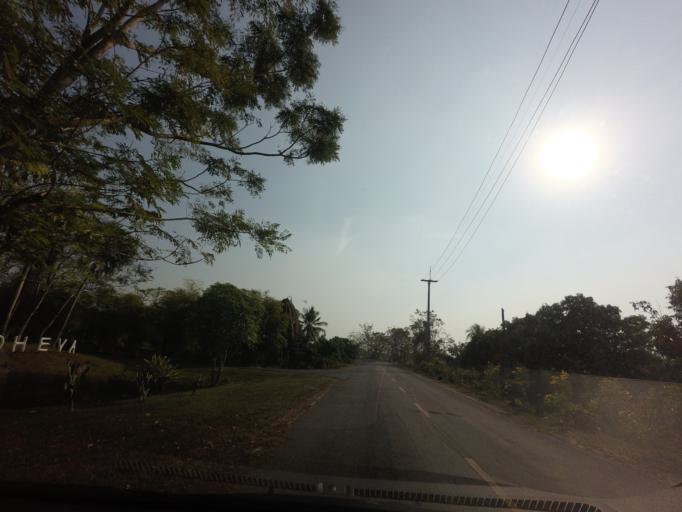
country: TH
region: Chachoengsao
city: Khlong Khuean
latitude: 13.7596
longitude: 101.1896
